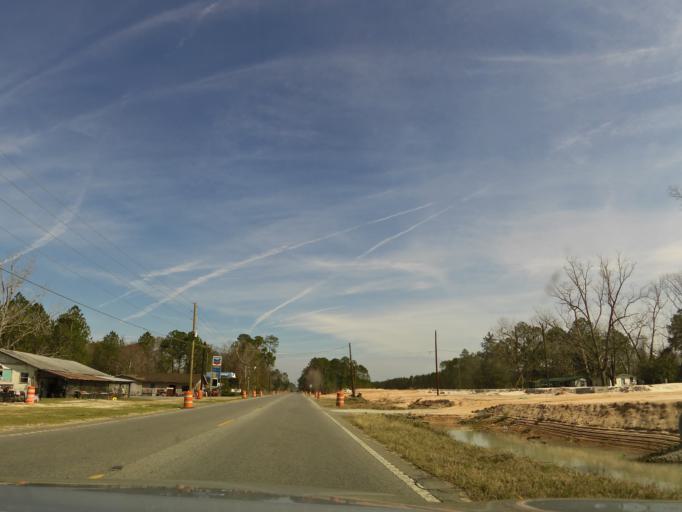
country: US
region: Georgia
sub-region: Ware County
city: Deenwood
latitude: 31.1834
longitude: -82.3969
